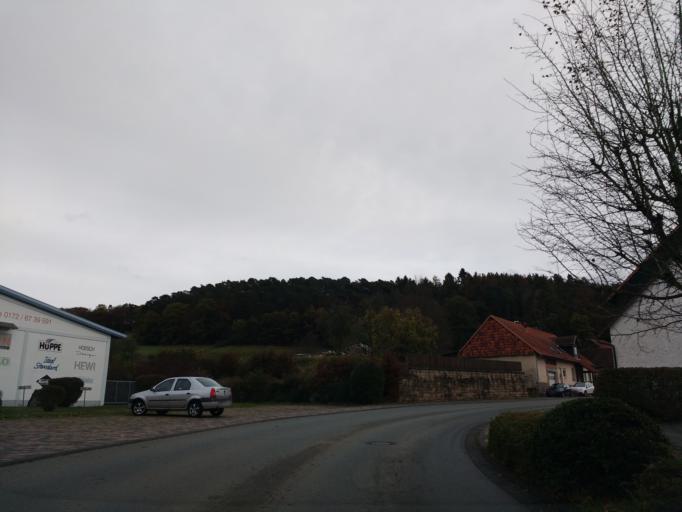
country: DE
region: Hesse
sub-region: Regierungsbezirk Kassel
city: Vohl
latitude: 51.2066
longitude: 8.9479
